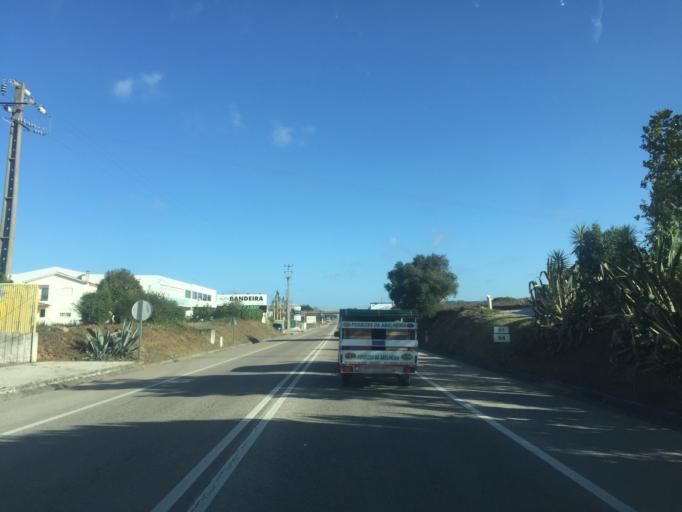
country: PT
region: Leiria
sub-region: Alcobaca
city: Benedita
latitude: 39.4299
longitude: -8.9585
